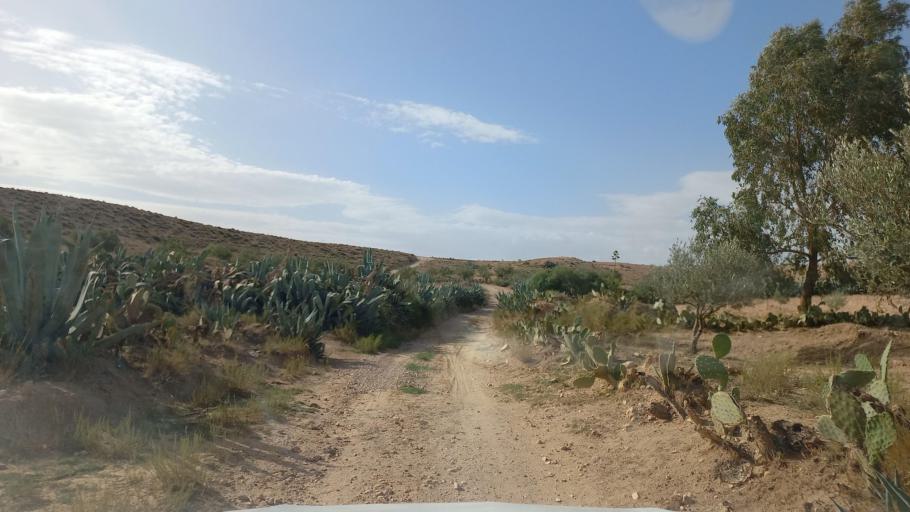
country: TN
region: Al Qasrayn
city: Kasserine
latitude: 35.2590
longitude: 8.9272
